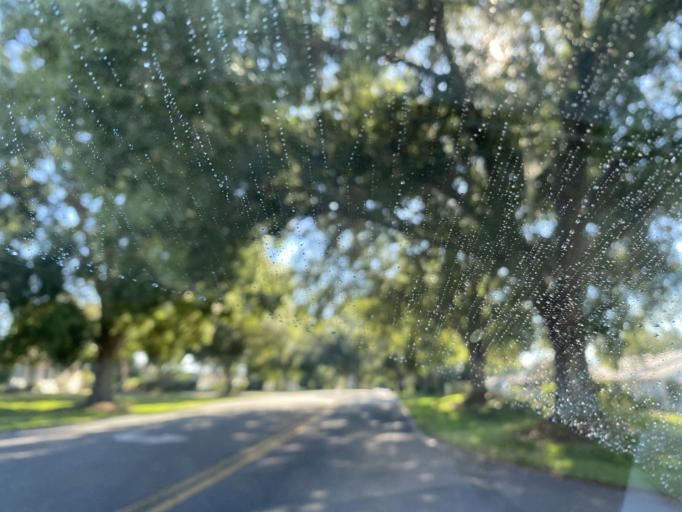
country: US
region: Florida
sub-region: Marion County
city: Ocala
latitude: 29.0543
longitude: -82.2598
